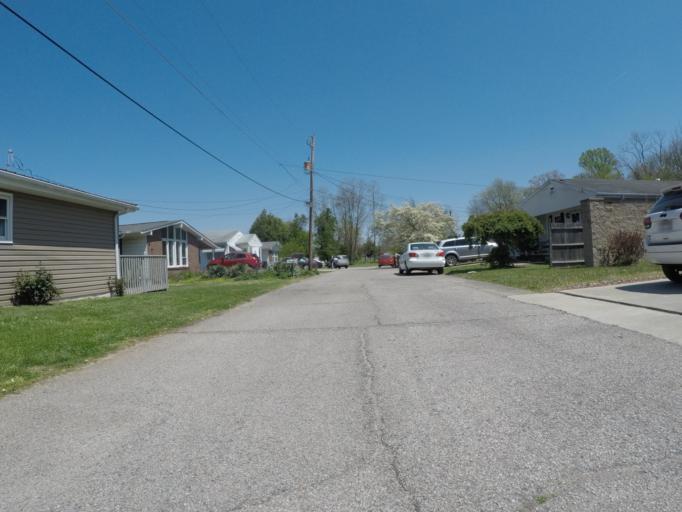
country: US
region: West Virginia
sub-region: Cabell County
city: Barboursville
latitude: 38.4120
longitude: -82.3069
